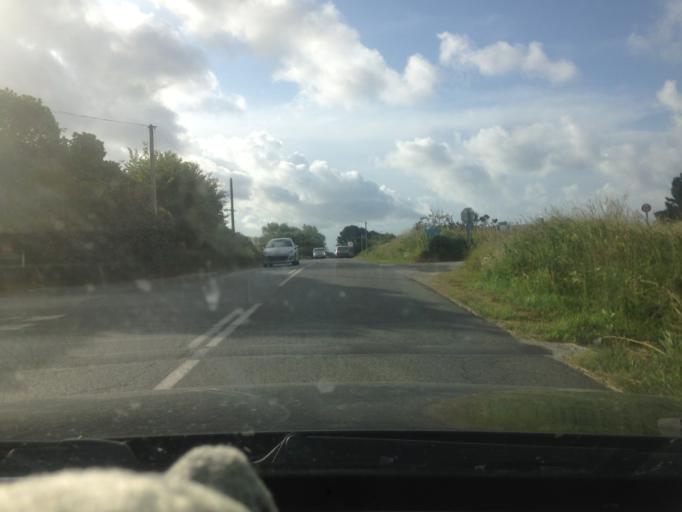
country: FR
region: Brittany
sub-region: Departement du Morbihan
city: Plouharnel
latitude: 47.5908
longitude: -3.0961
